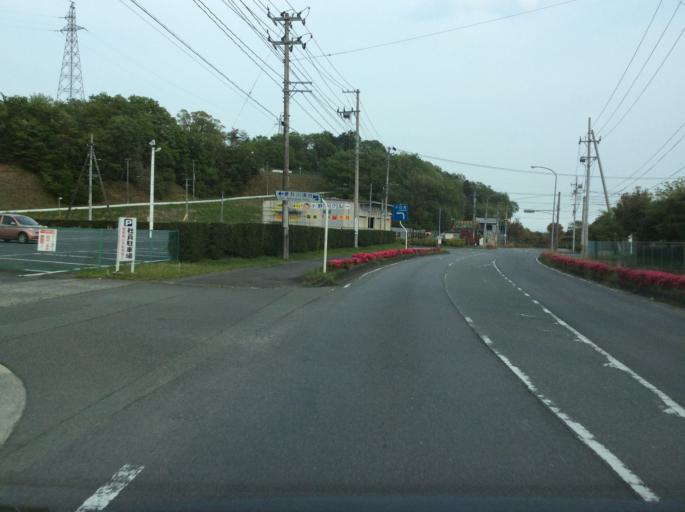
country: JP
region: Fukushima
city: Iwaki
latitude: 37.0778
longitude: 140.8538
